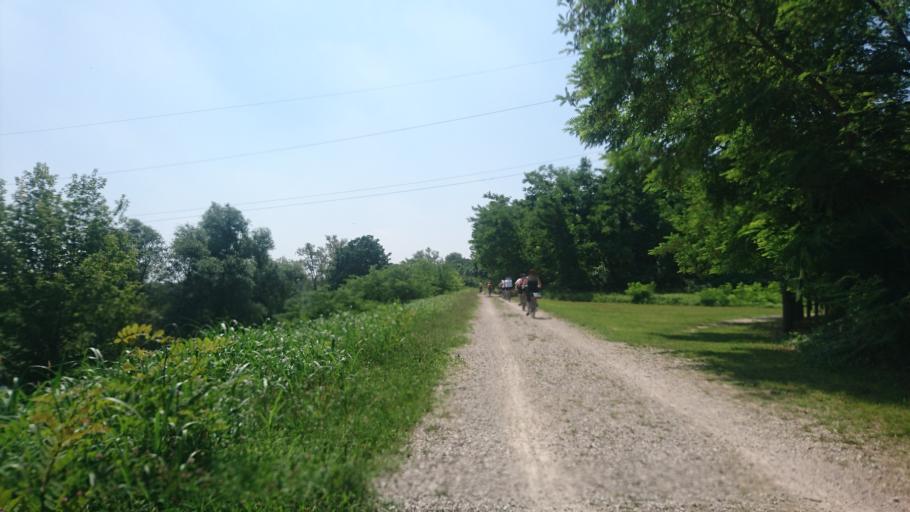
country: IT
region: Veneto
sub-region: Provincia di Venezia
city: Vigonovo
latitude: 45.3933
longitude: 12.0093
